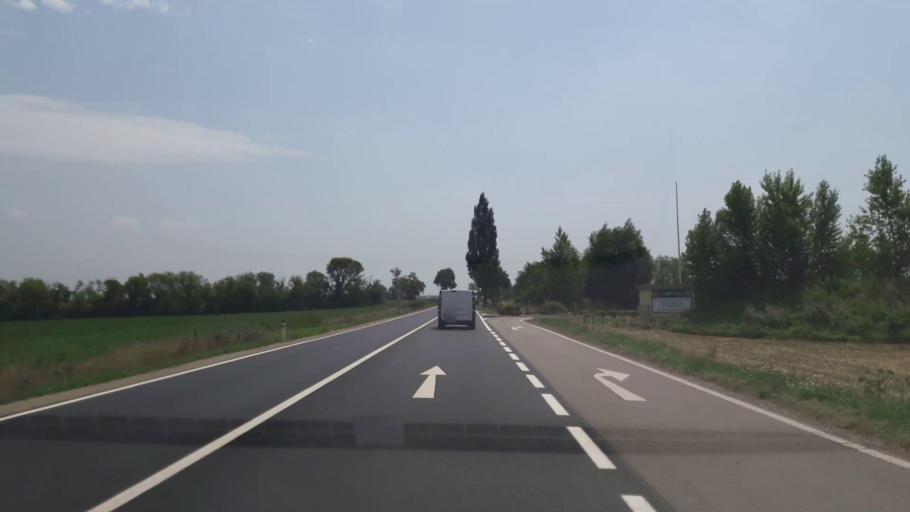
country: AT
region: Lower Austria
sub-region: Politischer Bezirk Wien-Umgebung
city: Schwechat
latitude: 48.1305
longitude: 16.4995
